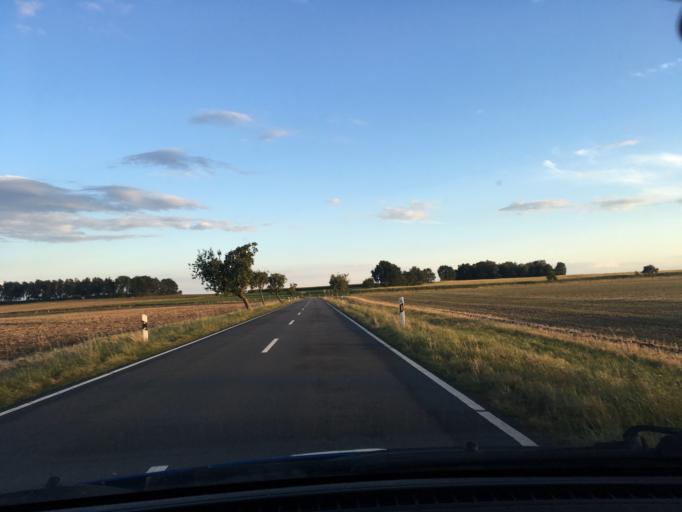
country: DE
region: Lower Saxony
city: Bergen
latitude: 52.7752
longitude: 10.0076
